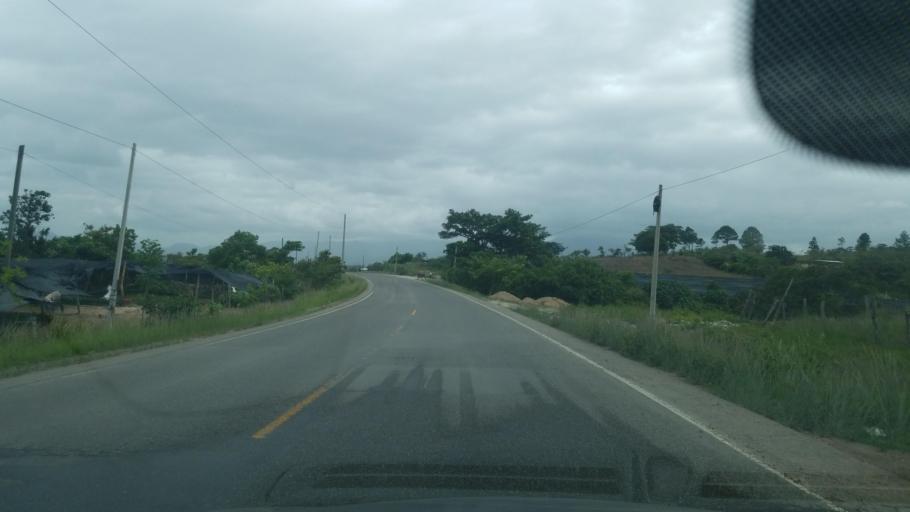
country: HN
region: Ocotepeque
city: Lucerna
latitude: 14.5664
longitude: -88.9322
